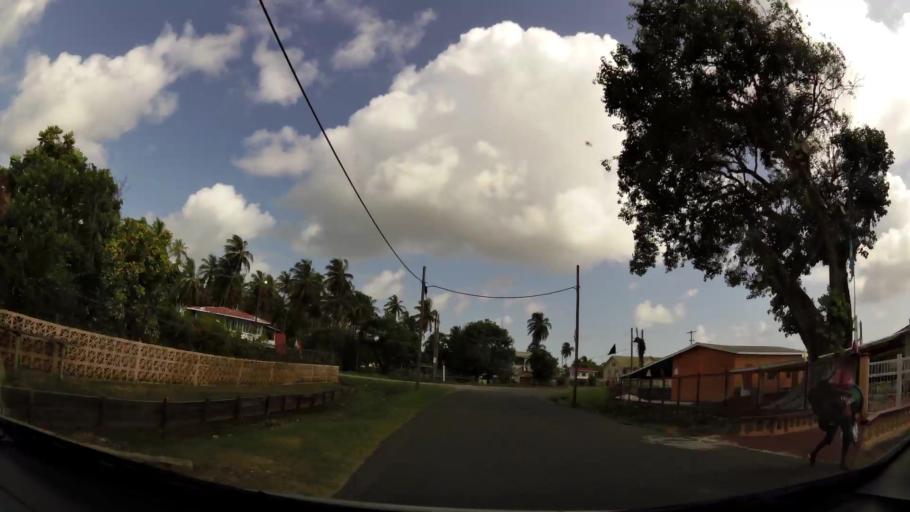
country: GY
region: Demerara-Mahaica
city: Mahaica Village
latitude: 6.7133
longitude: -57.9301
